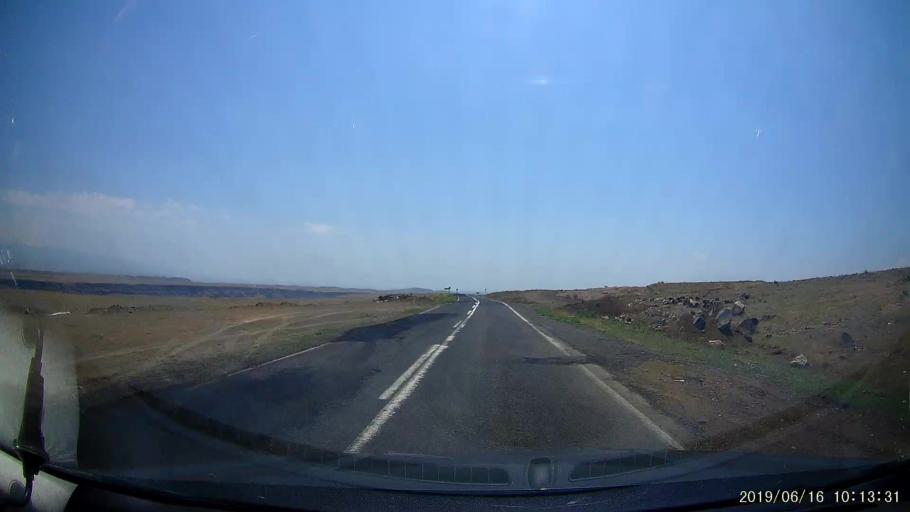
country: TR
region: Igdir
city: Tuzluca
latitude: 40.1922
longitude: 43.6444
